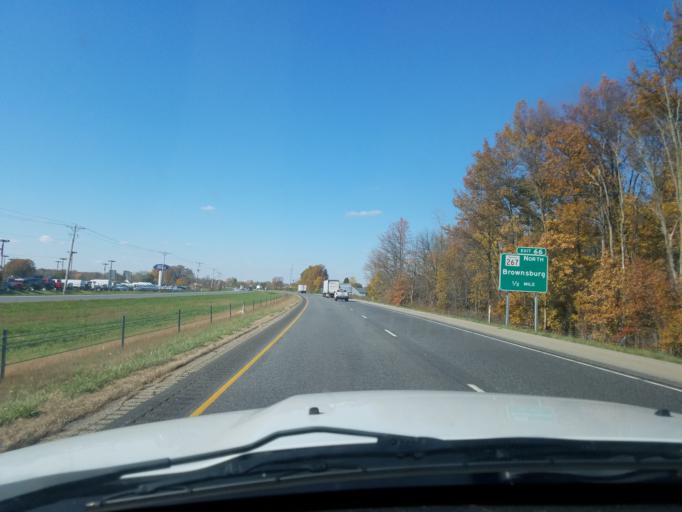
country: US
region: Indiana
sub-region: Hendricks County
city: Brownsburg
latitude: 39.8565
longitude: -86.3812
